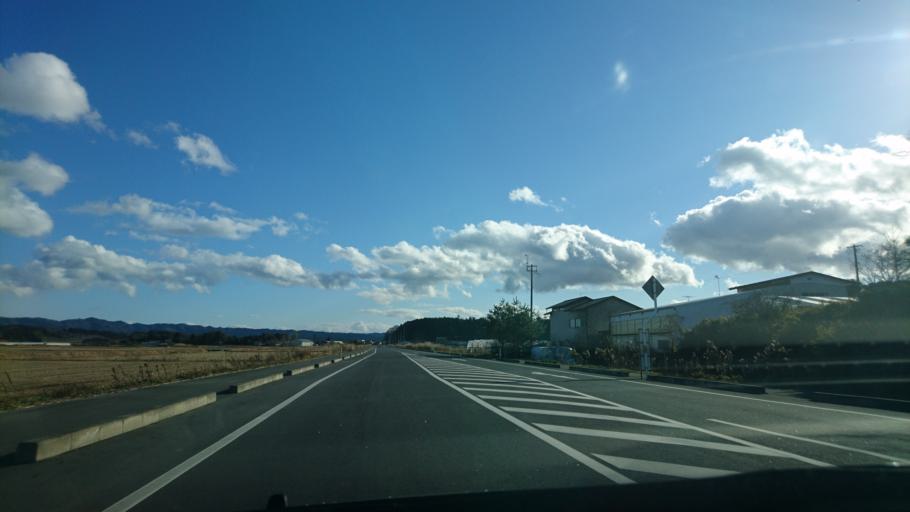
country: JP
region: Iwate
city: Ichinoseki
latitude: 38.7395
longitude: 141.2563
